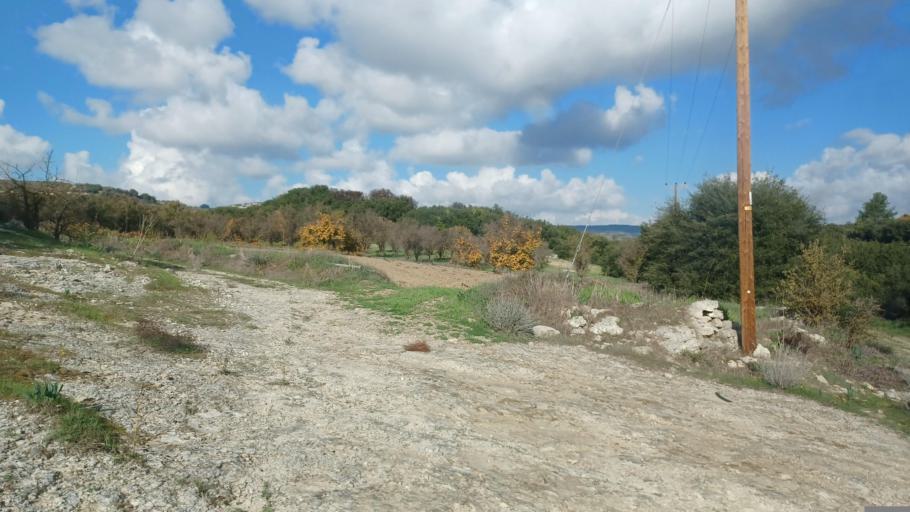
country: CY
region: Pafos
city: Mesogi
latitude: 34.8414
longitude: 32.5485
